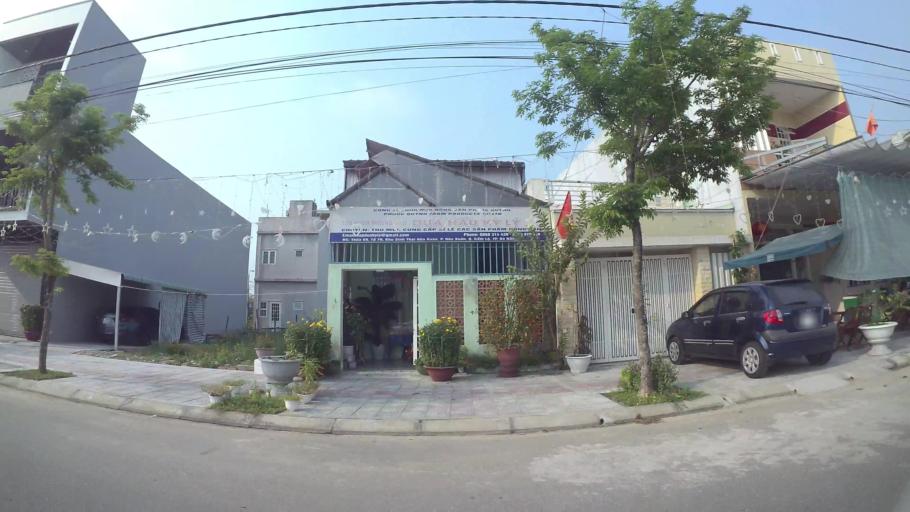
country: VN
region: Da Nang
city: Cam Le
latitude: 16.0077
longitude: 108.2240
